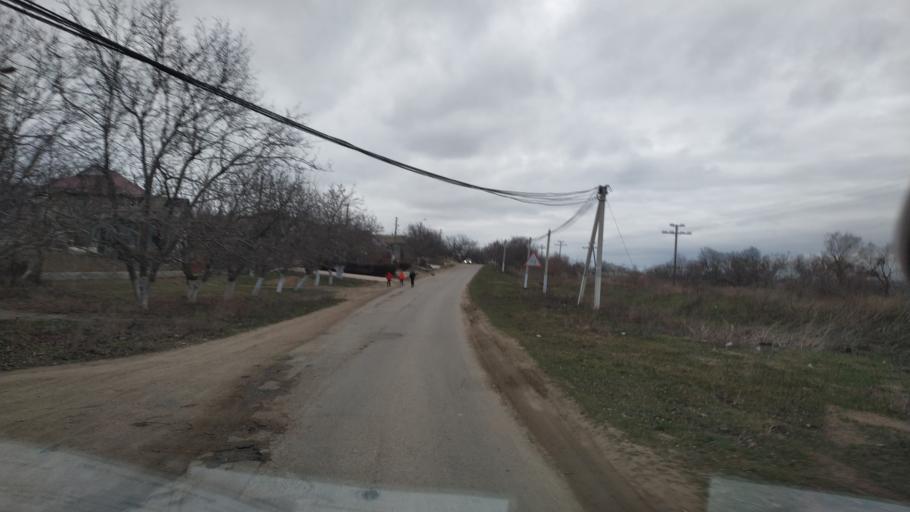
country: MD
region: Bender
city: Bender
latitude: 46.7695
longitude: 29.4815
